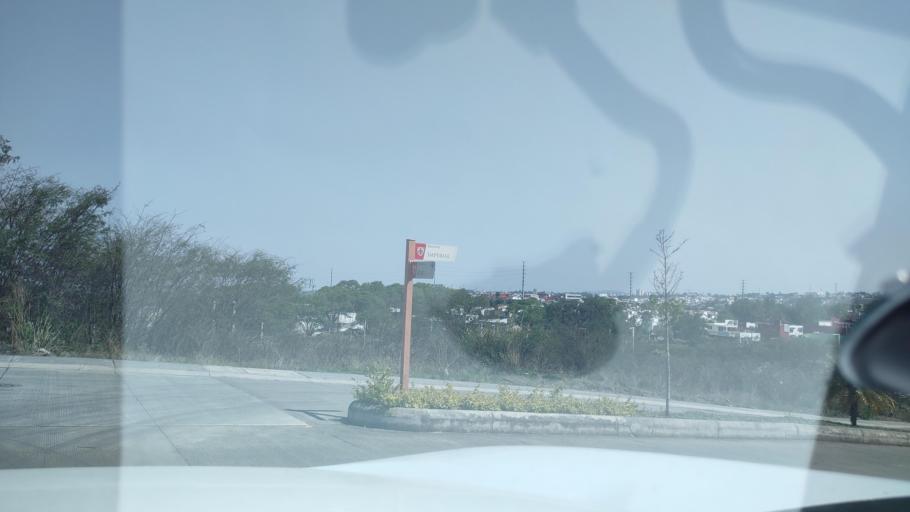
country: MX
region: Veracruz
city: El Castillo
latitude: 19.5281
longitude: -96.8696
